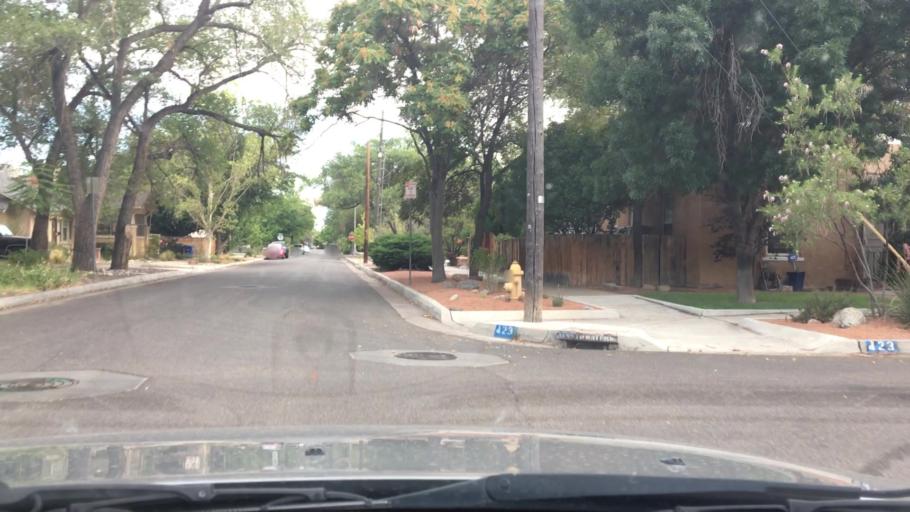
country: US
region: New Mexico
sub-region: Bernalillo County
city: Albuquerque
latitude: 35.0914
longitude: -106.6612
